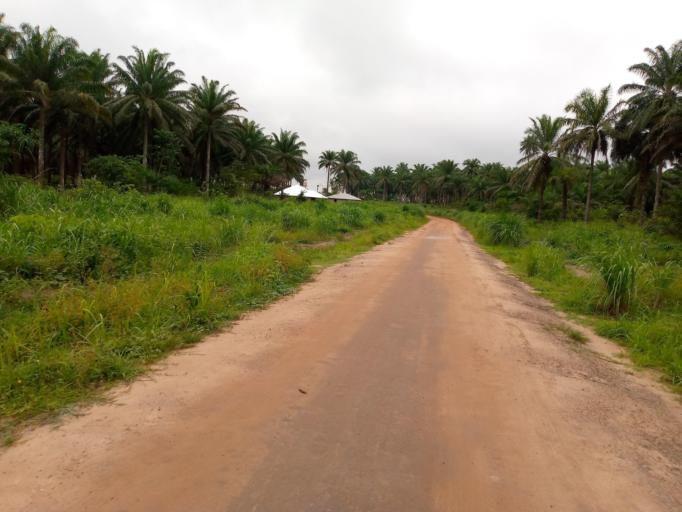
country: SL
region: Southern Province
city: Sumbuya
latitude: 7.5700
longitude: -12.0897
